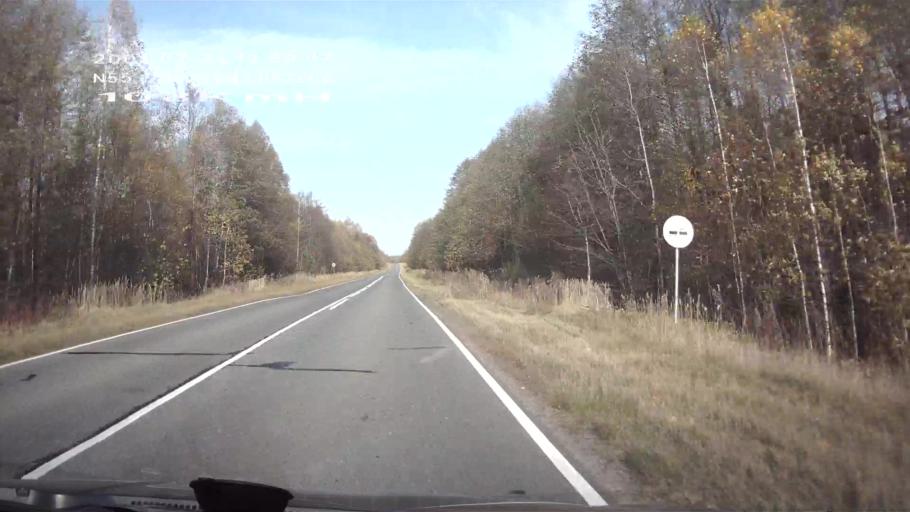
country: RU
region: Chuvashia
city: Buinsk
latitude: 55.1789
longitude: 47.0632
